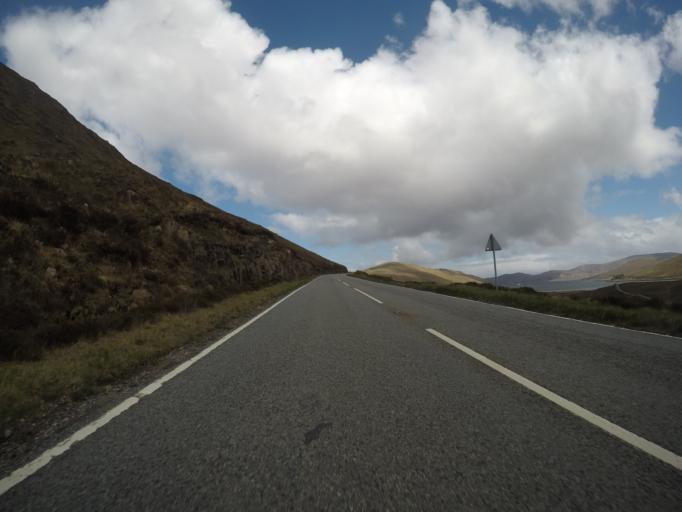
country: GB
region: Scotland
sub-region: Highland
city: Portree
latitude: 57.2662
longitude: -6.0904
